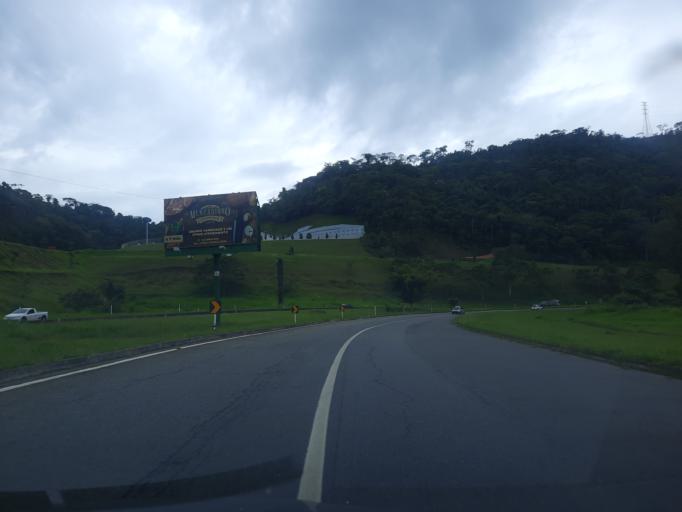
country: BR
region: Rio de Janeiro
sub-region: Petropolis
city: Petropolis
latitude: -22.4085
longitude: -43.1486
